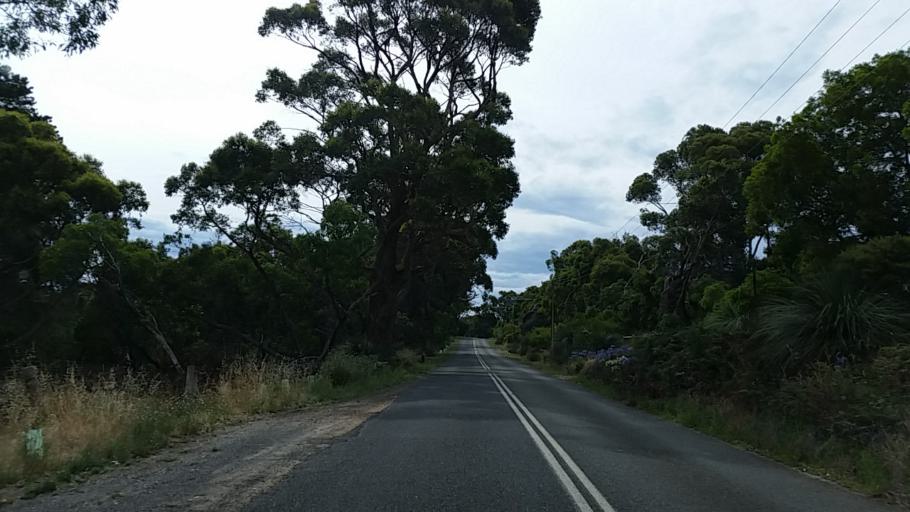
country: AU
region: South Australia
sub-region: Yankalilla
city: Normanville
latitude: -35.4154
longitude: 138.4289
